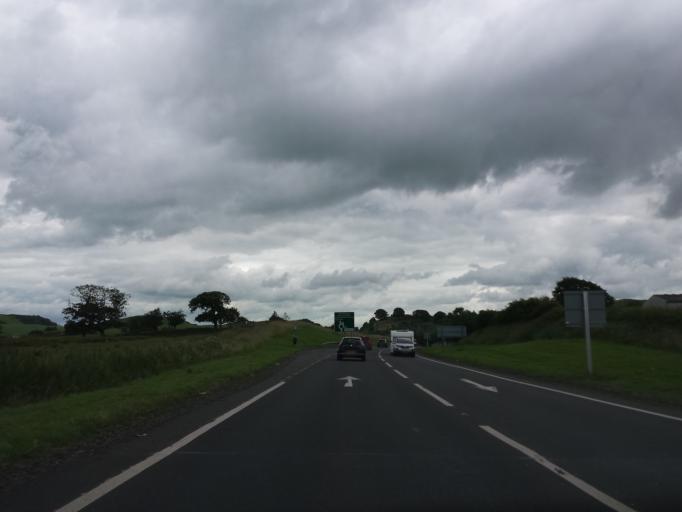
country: GB
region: Scotland
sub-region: Dumfries and Galloway
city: Dumfries
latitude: 55.0554
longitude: -3.7238
